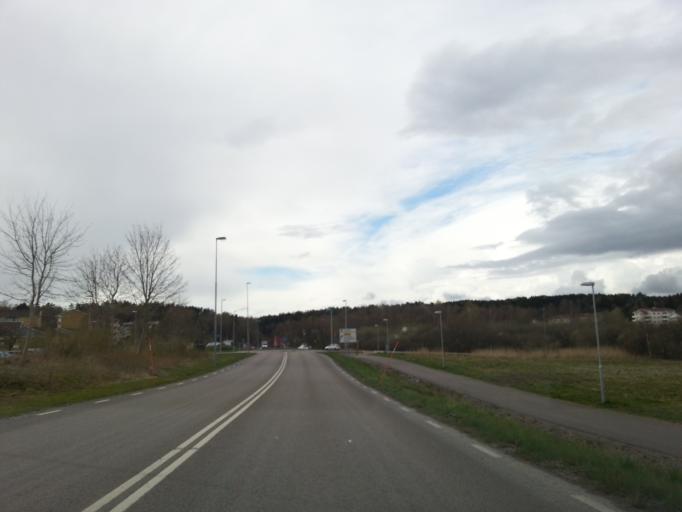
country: SE
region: Vaestra Goetaland
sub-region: Kungalvs Kommun
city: Kungalv
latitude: 57.8862
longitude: 11.9677
